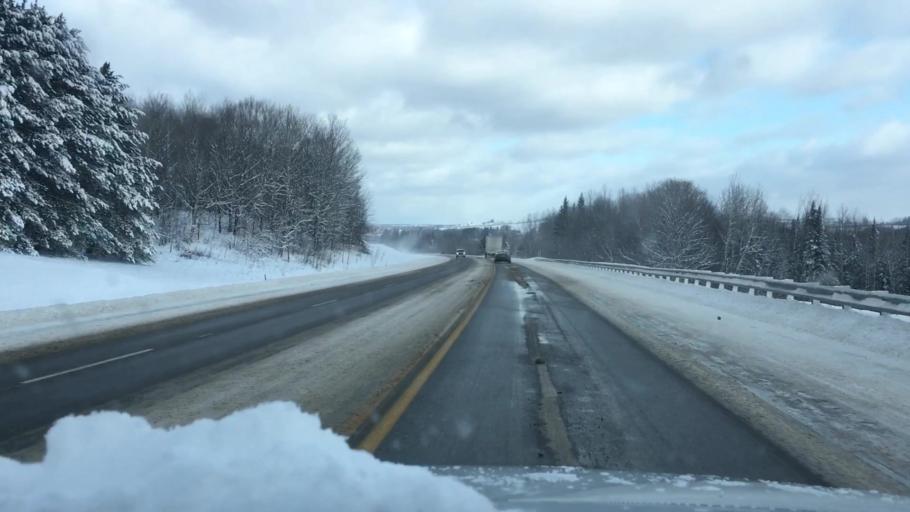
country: US
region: Maine
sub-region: Aroostook County
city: Caribou
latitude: 46.8223
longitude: -67.9935
